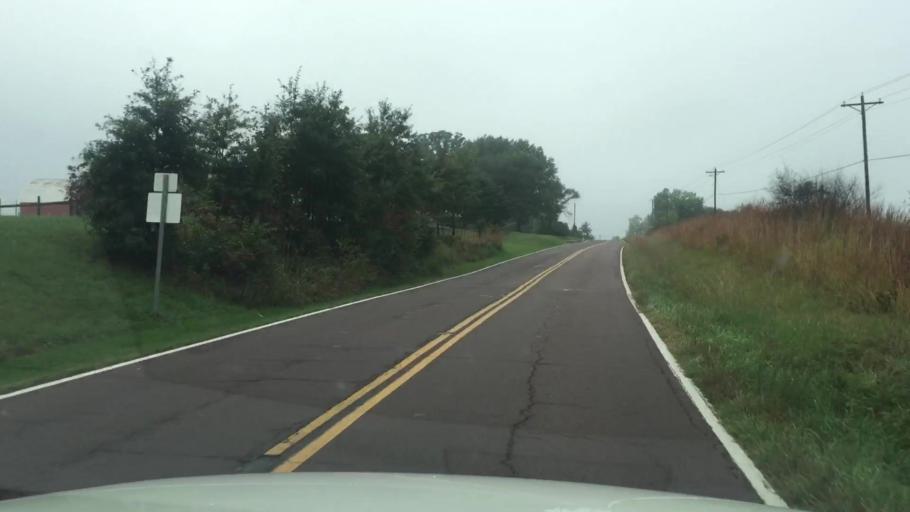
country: US
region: Missouri
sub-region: Boone County
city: Columbia
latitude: 38.8607
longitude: -92.3181
